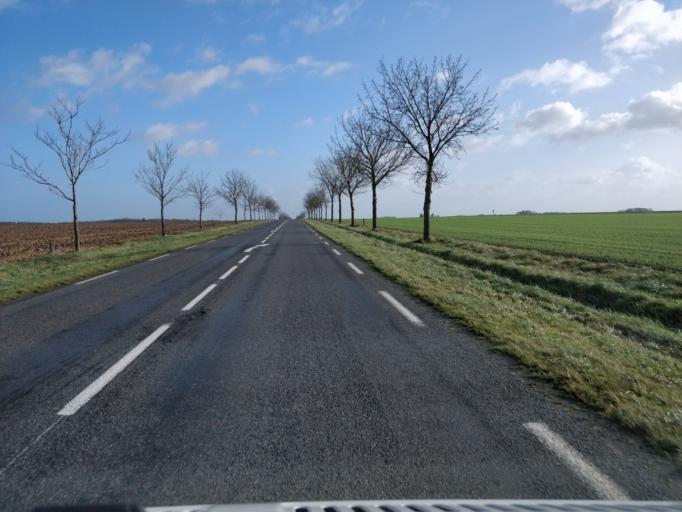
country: FR
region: Ile-de-France
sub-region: Departement de Seine-et-Marne
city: Lorrez-le-Bocage-Preaux
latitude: 48.2100
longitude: 2.9450
